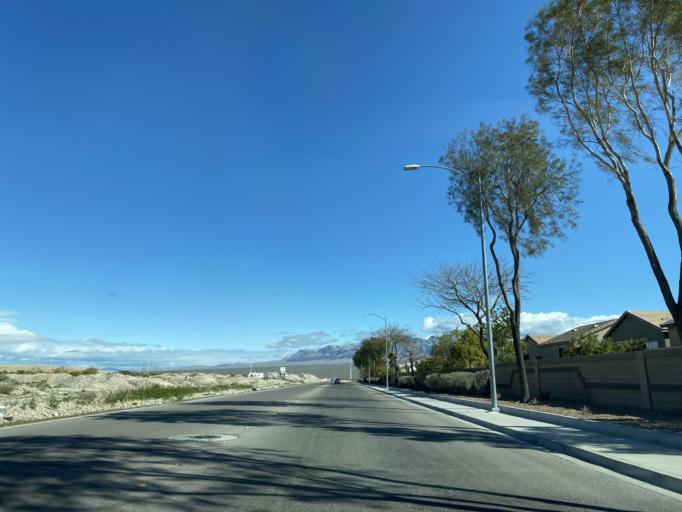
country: US
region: Nevada
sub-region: Clark County
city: Summerlin South
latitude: 36.3259
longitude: -115.2966
